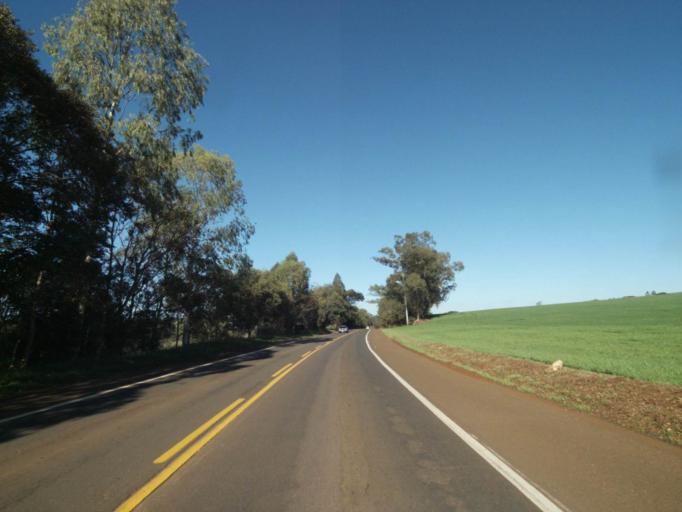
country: BR
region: Parana
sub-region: Faxinal
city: Faxinal
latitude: -23.7555
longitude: -51.1371
